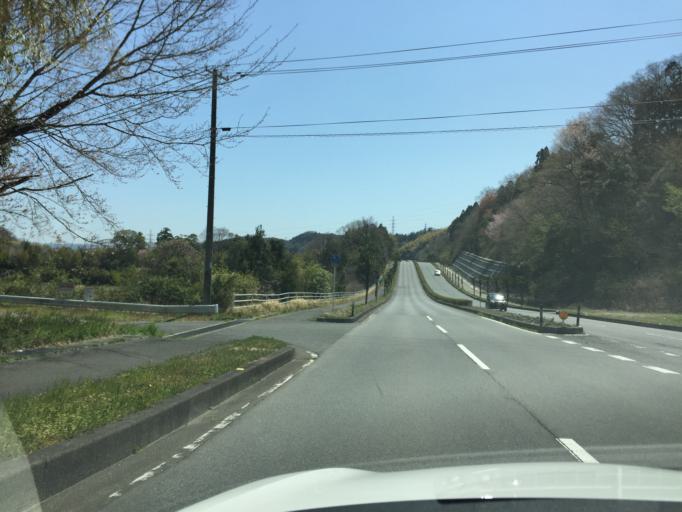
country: JP
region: Fukushima
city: Iwaki
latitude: 36.9868
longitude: 140.8273
